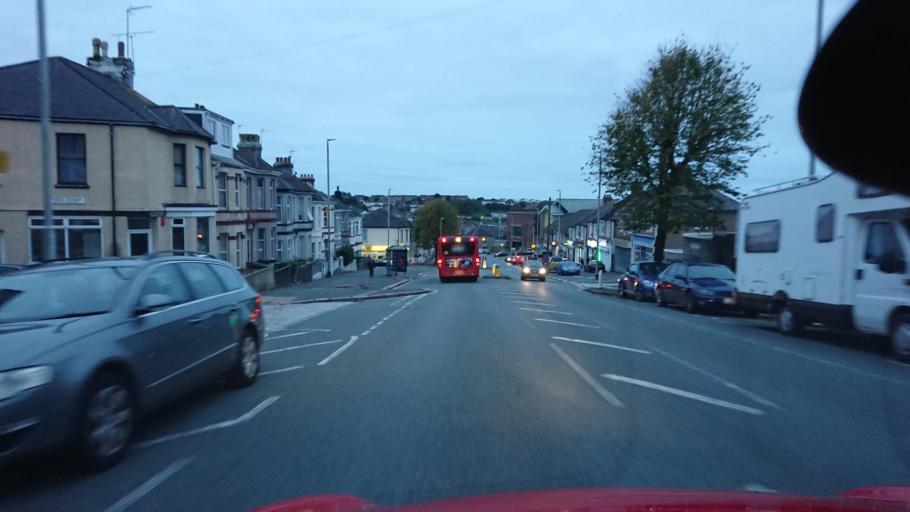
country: GB
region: England
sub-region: Cornwall
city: Torpoint
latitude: 50.4064
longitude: -4.1863
